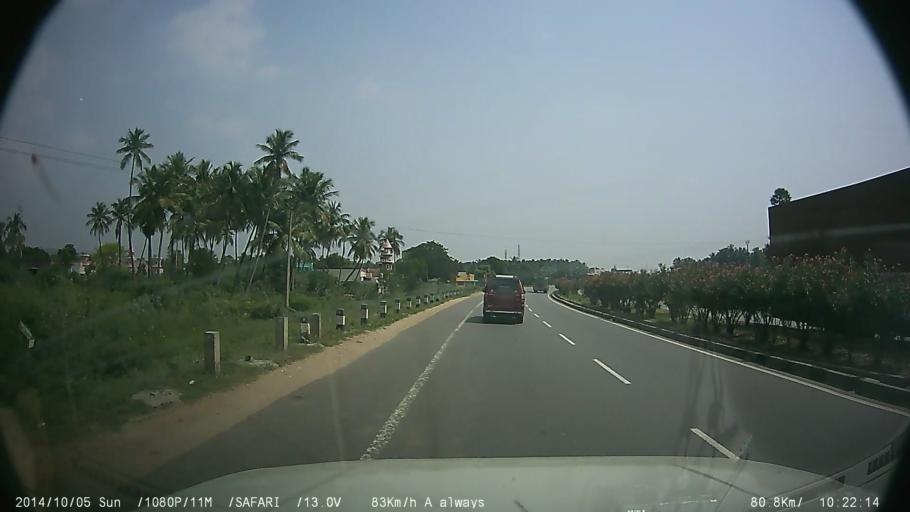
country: IN
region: Tamil Nadu
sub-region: Salem
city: Salem
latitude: 11.6071
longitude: 78.0976
